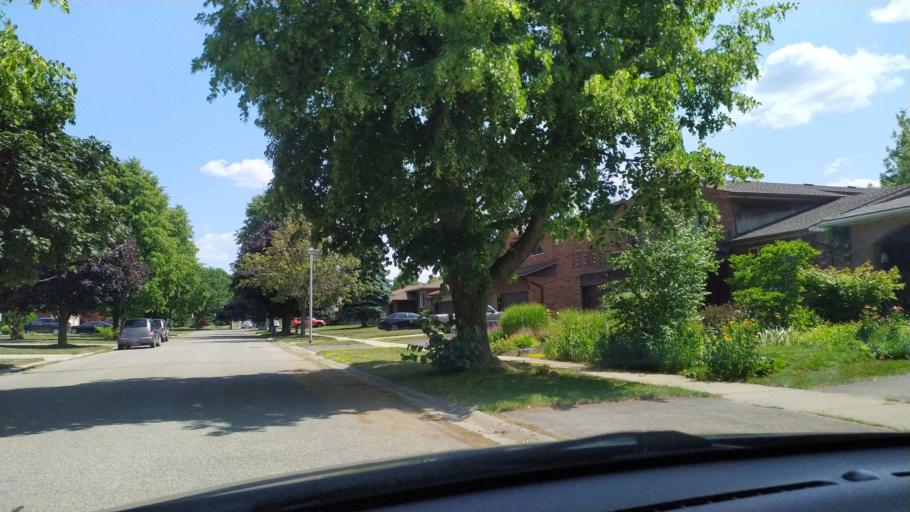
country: CA
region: Ontario
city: Stratford
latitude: 43.3633
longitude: -81.0043
